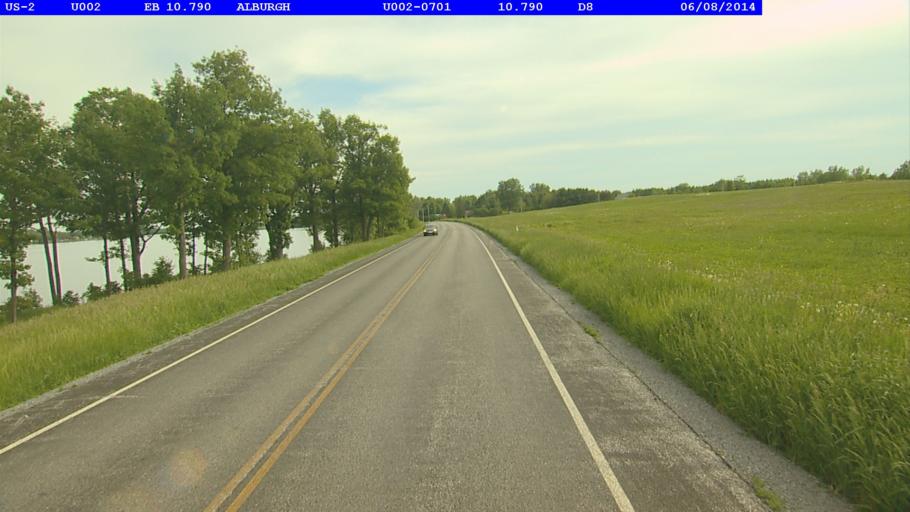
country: US
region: Vermont
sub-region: Grand Isle County
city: North Hero
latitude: 44.8976
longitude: -73.2757
